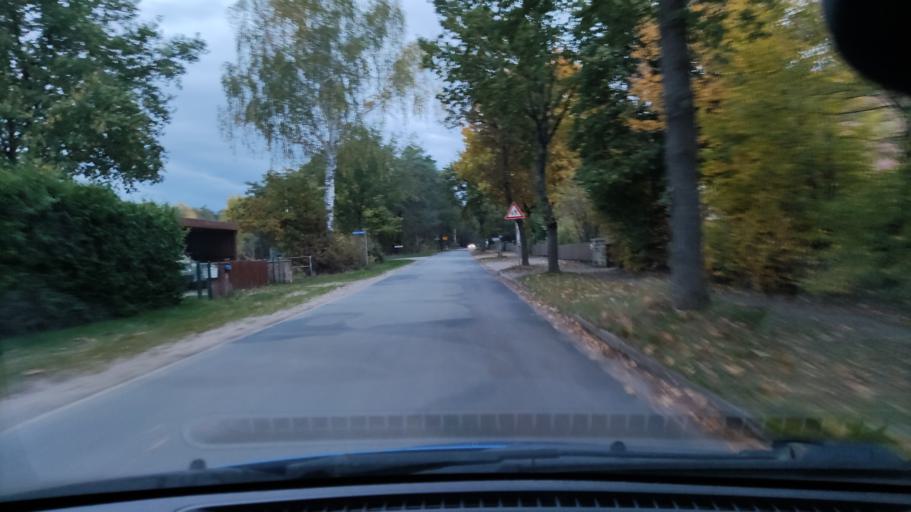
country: DE
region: Lower Saxony
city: Prezelle
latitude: 52.9648
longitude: 11.4002
